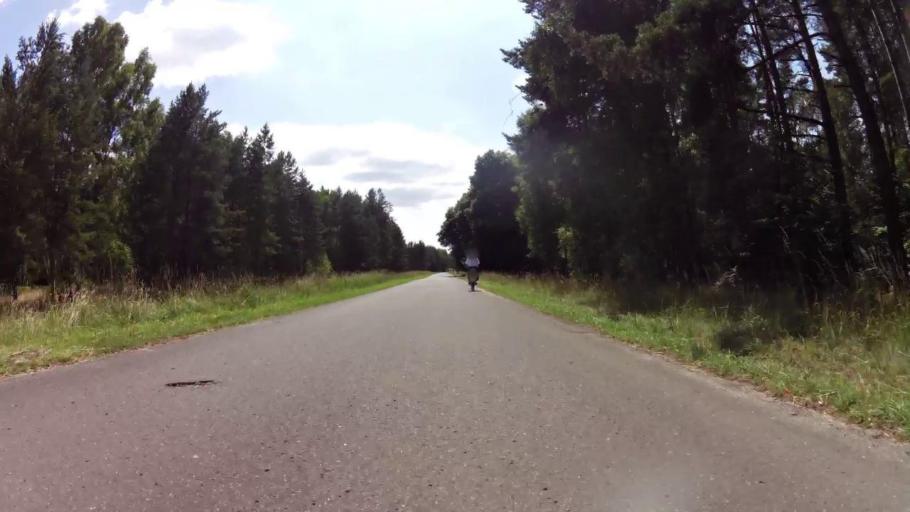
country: PL
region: West Pomeranian Voivodeship
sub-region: Powiat choszczenski
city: Drawno
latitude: 53.3818
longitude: 15.7290
